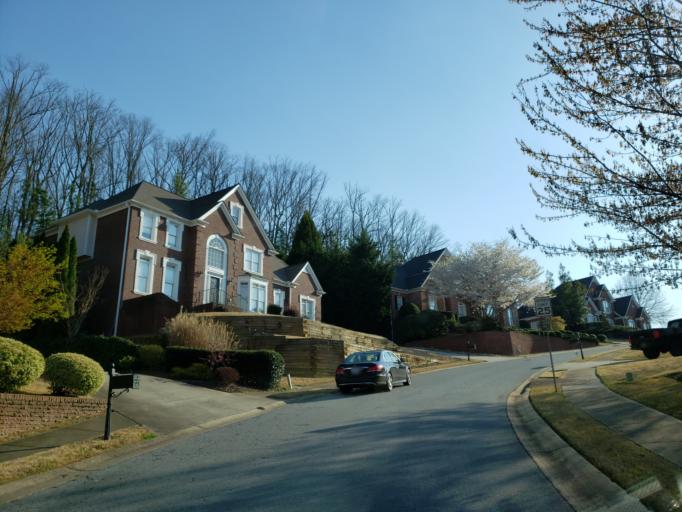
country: US
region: Georgia
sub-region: Cobb County
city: Marietta
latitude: 33.9822
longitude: -84.5085
